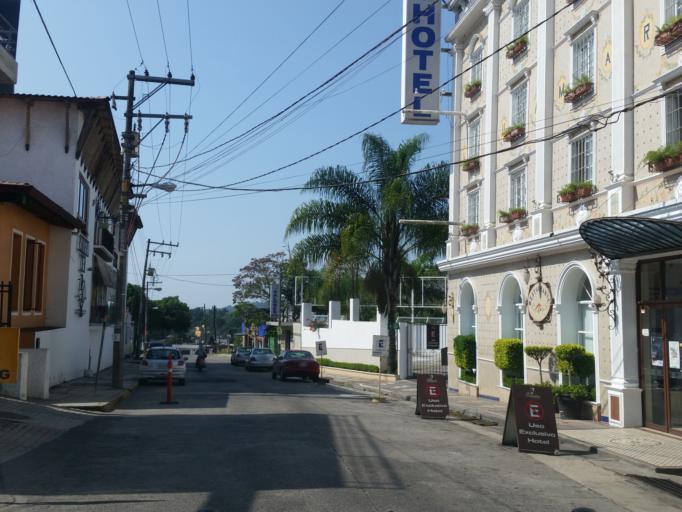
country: MX
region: Veracruz
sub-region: Xalapa
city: Xalapa de Enriquez
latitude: 19.5248
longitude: -96.9037
